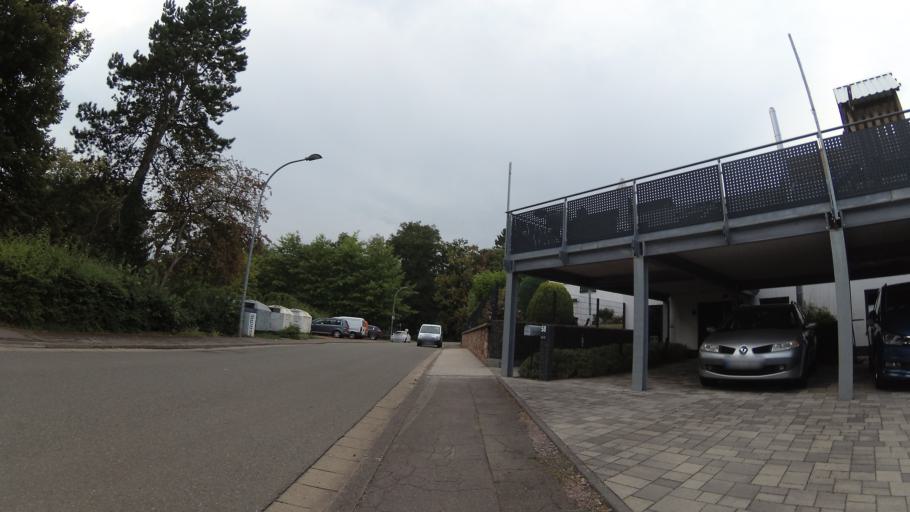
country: DE
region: Saarland
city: Sulzbach
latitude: 49.2806
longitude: 7.0640
